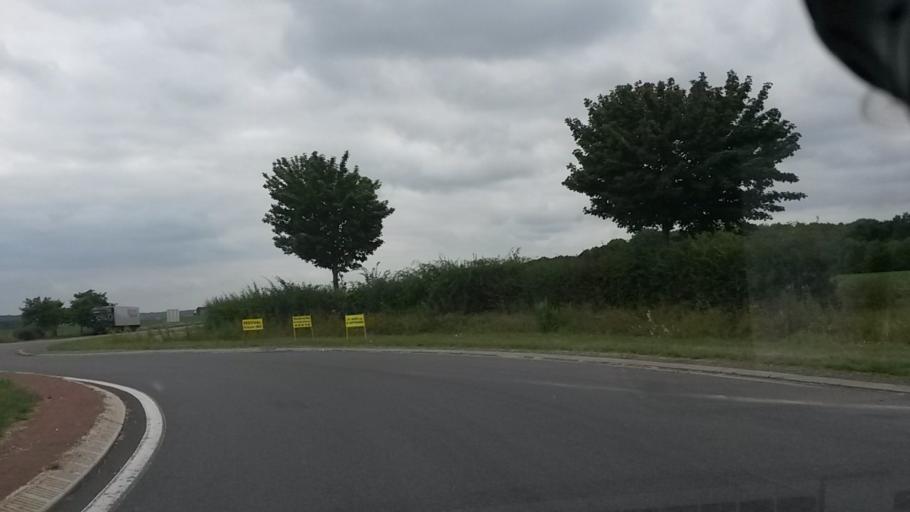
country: FR
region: Picardie
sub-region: Departement de la Somme
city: Saleux
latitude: 49.8606
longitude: 2.2109
